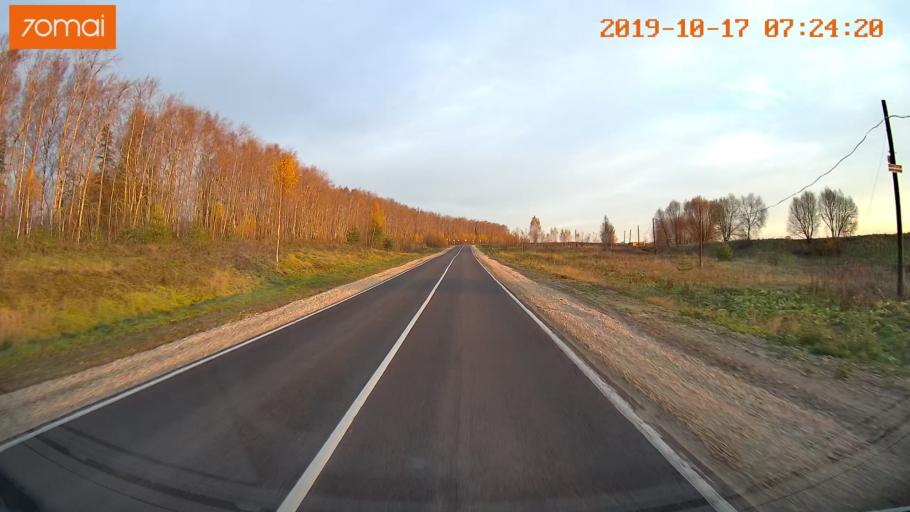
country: RU
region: Ivanovo
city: Gavrilov Posad
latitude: 56.3373
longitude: 40.1125
